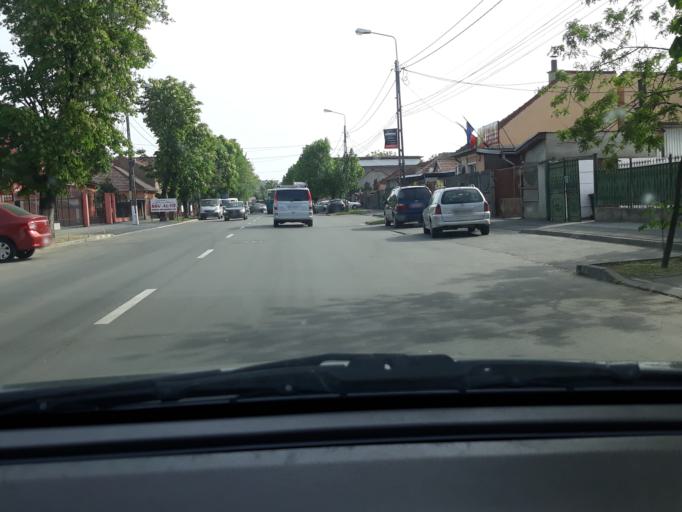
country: RO
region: Bihor
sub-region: Comuna Biharea
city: Oradea
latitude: 47.0423
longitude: 21.9558
